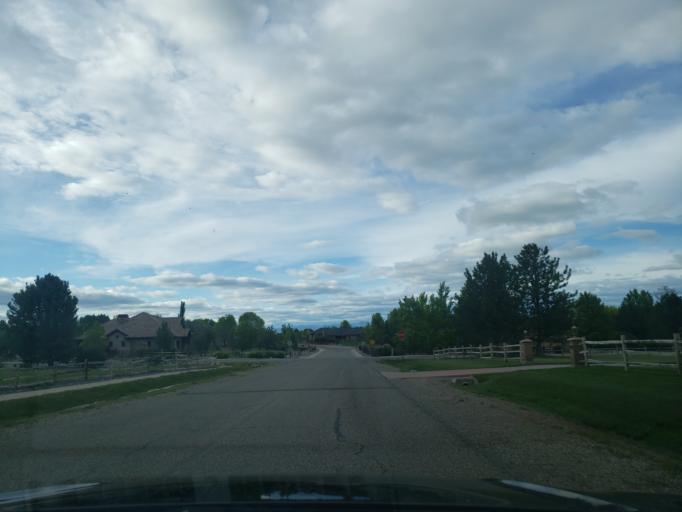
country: US
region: Colorado
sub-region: Mesa County
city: Redlands
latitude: 39.1057
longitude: -108.6746
